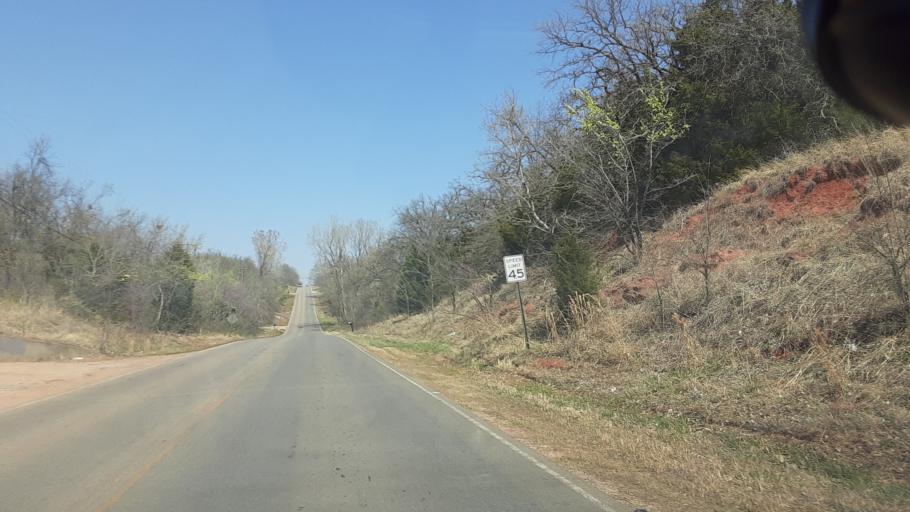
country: US
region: Oklahoma
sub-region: Oklahoma County
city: Edmond
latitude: 35.7547
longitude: -97.4784
